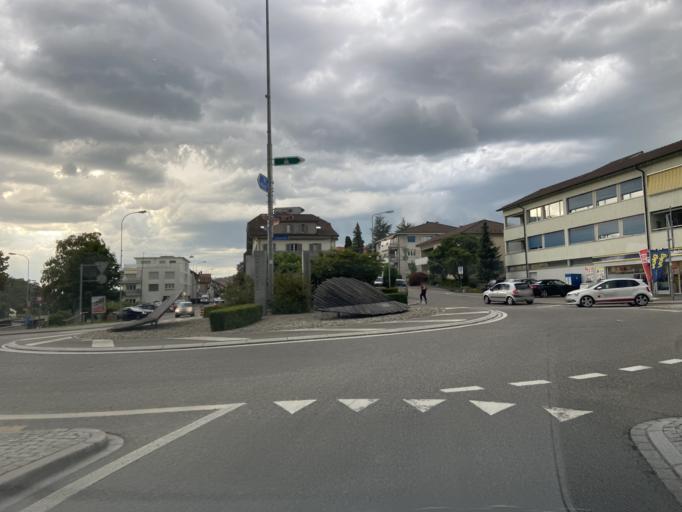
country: CH
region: Thurgau
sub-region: Muenchwilen District
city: Aadorf
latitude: 47.4882
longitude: 8.9039
